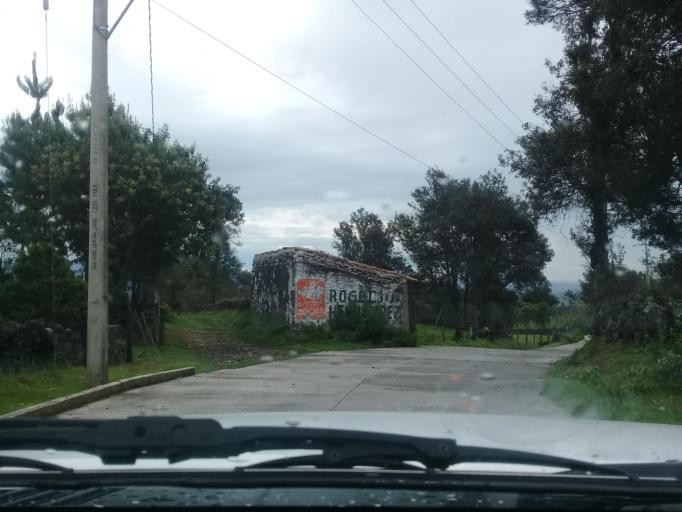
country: MX
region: Veracruz
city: Rafael Lucio
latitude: 19.6159
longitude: -96.9971
